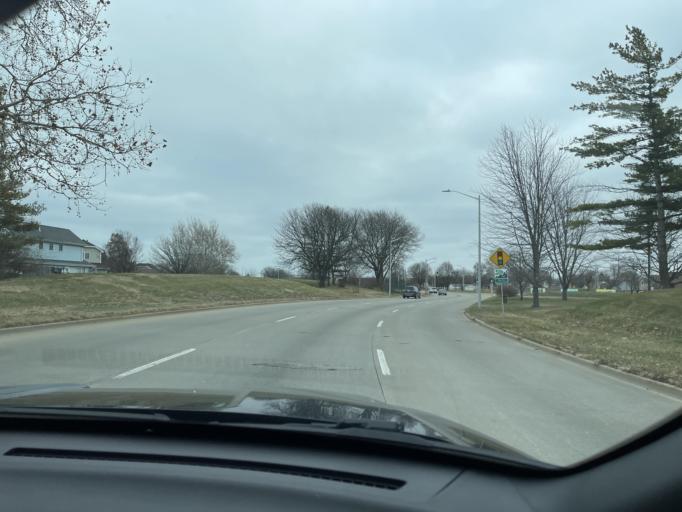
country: US
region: Illinois
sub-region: Sangamon County
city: Springfield
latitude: 39.8038
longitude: -89.6403
